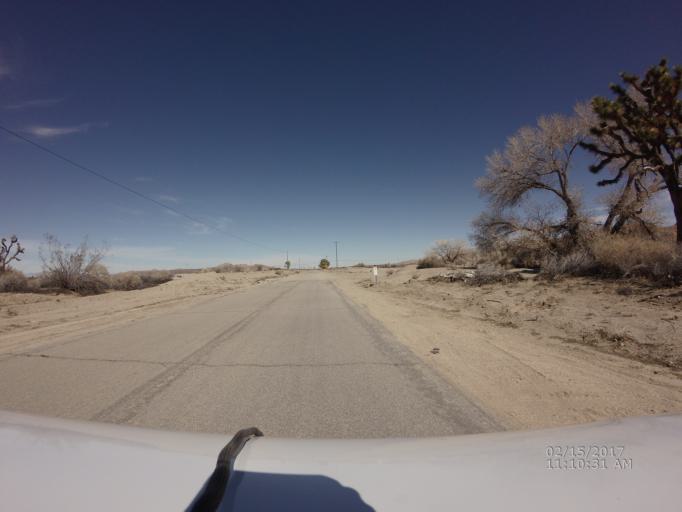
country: US
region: California
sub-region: Los Angeles County
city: Lake Los Angeles
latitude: 34.5851
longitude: -117.8807
